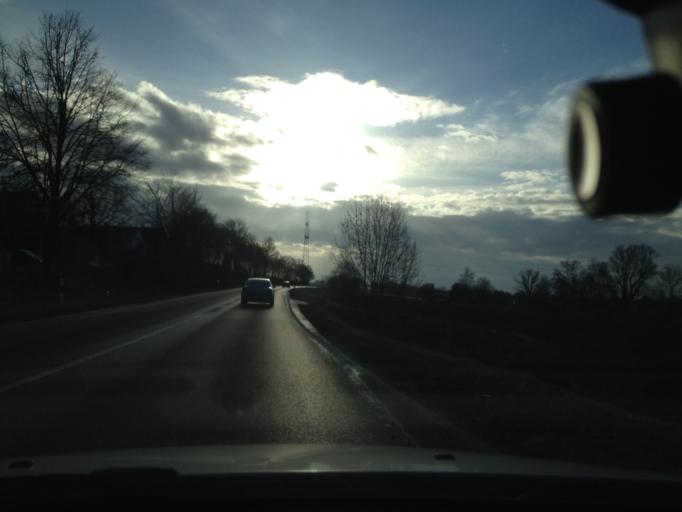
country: DE
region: Bavaria
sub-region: Swabia
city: Wehringen
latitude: 48.2411
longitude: 10.7957
